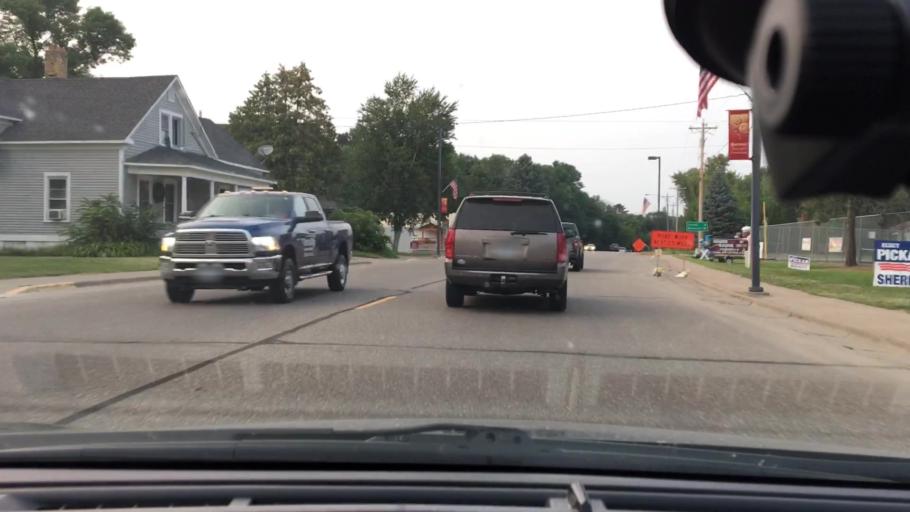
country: US
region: Minnesota
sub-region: Crow Wing County
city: Crosby
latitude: 46.4756
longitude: -93.9015
